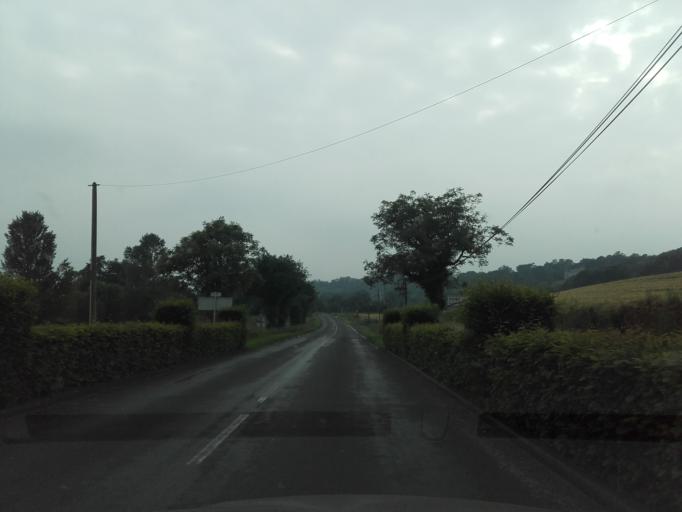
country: FR
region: Pays de la Loire
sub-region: Departement de la Sarthe
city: Ruille-sur-Loir
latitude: 47.7709
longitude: 0.6888
